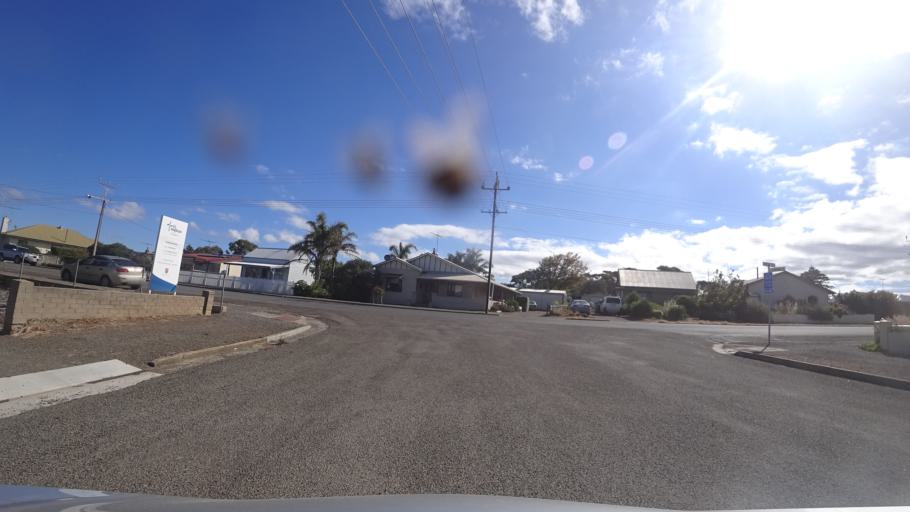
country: AU
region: South Australia
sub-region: Kangaroo Island
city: Kingscote
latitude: -35.6560
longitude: 137.6374
